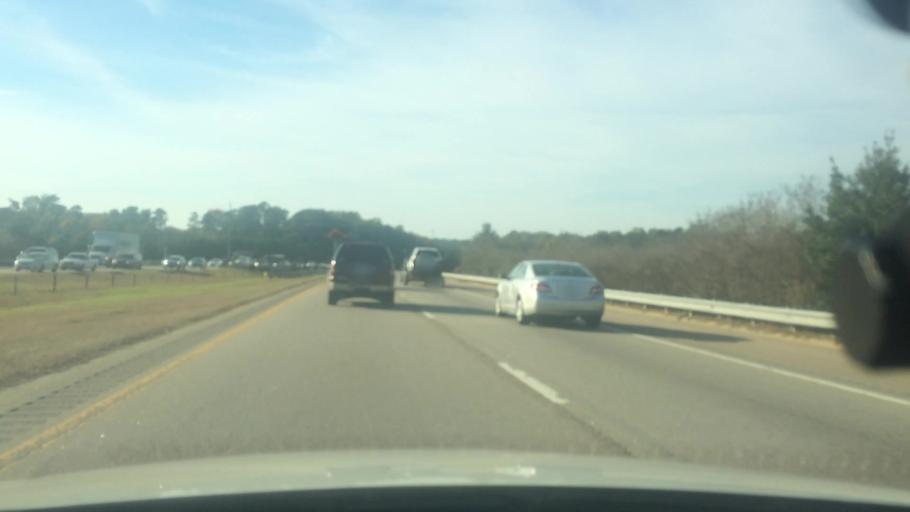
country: US
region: North Carolina
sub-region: Wake County
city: West Raleigh
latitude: 35.8070
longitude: -78.7215
